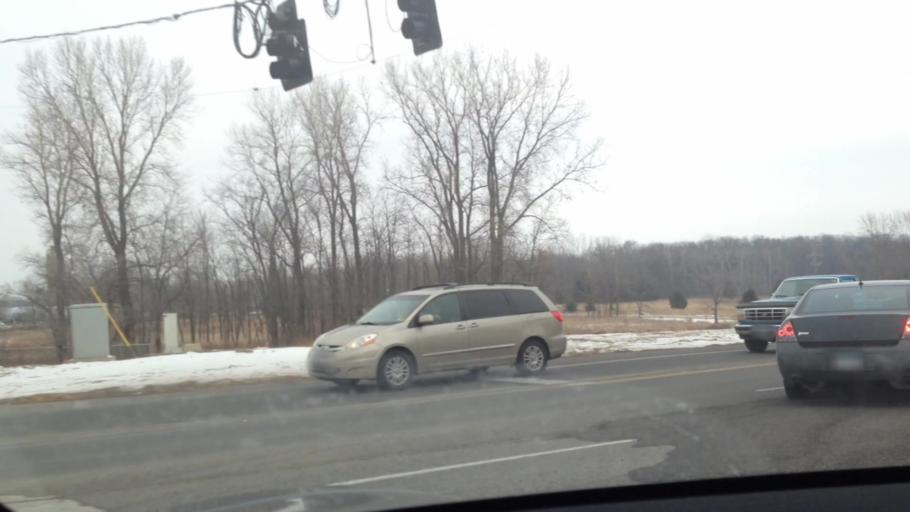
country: US
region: Minnesota
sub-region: Anoka County
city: Columbus
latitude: 45.2505
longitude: -93.0231
